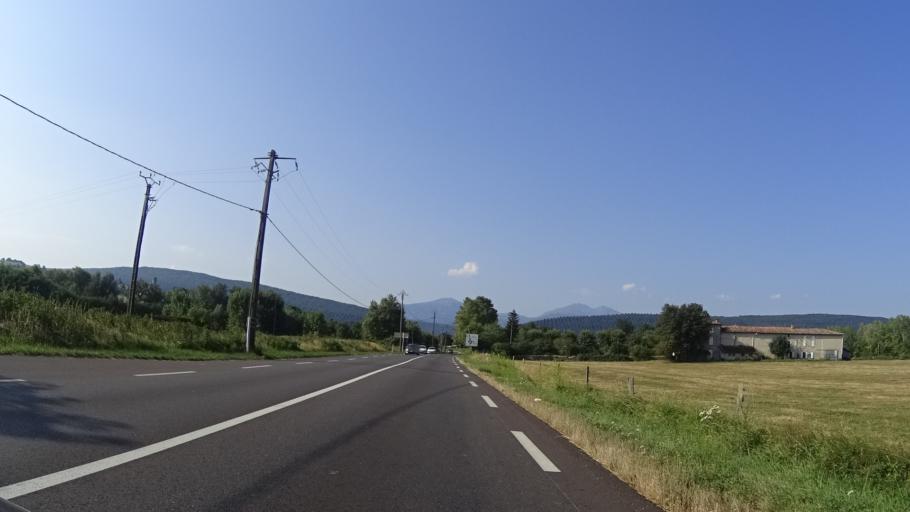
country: FR
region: Midi-Pyrenees
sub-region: Departement de l'Ariege
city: Lavelanet
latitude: 42.9798
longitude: 1.8689
